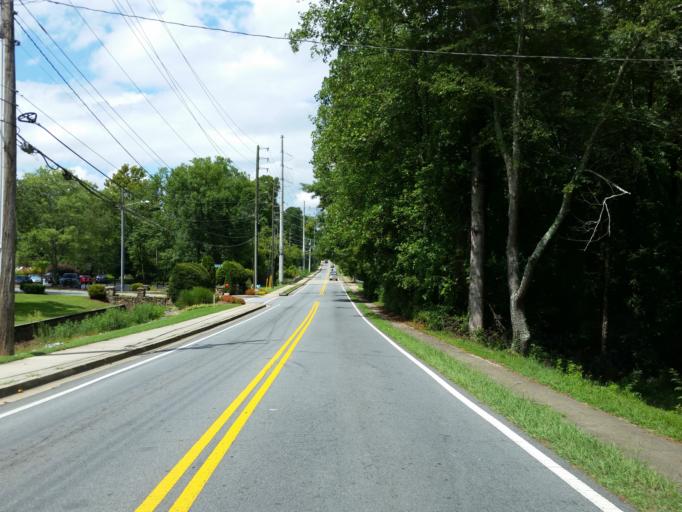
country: US
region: Georgia
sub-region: Cobb County
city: Marietta
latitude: 33.9522
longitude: -84.4780
